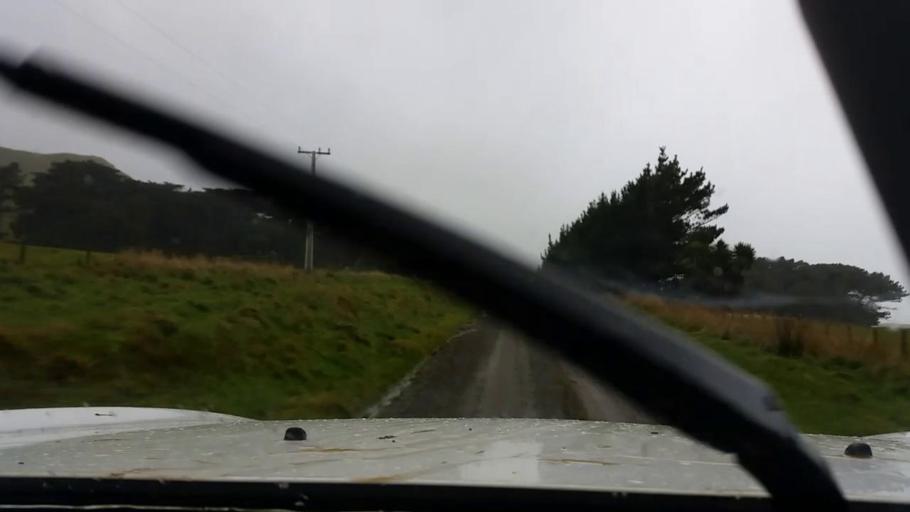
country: NZ
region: Wellington
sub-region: Masterton District
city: Masterton
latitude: -41.2586
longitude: 175.9011
